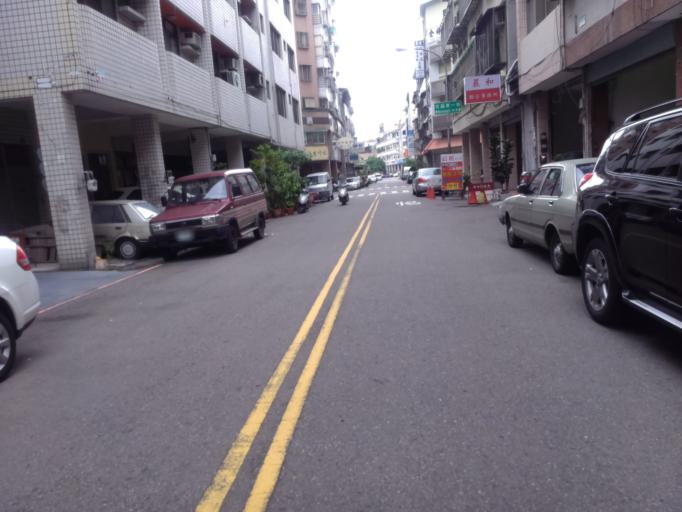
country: TW
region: Taiwan
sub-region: Taichung City
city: Taichung
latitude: 24.1722
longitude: 120.6778
